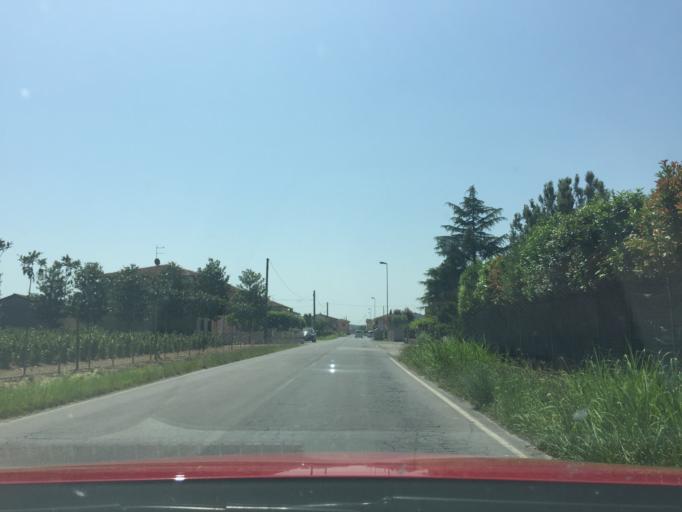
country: IT
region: Tuscany
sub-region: Provincia di Pistoia
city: Anchione
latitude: 43.8323
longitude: 10.7539
